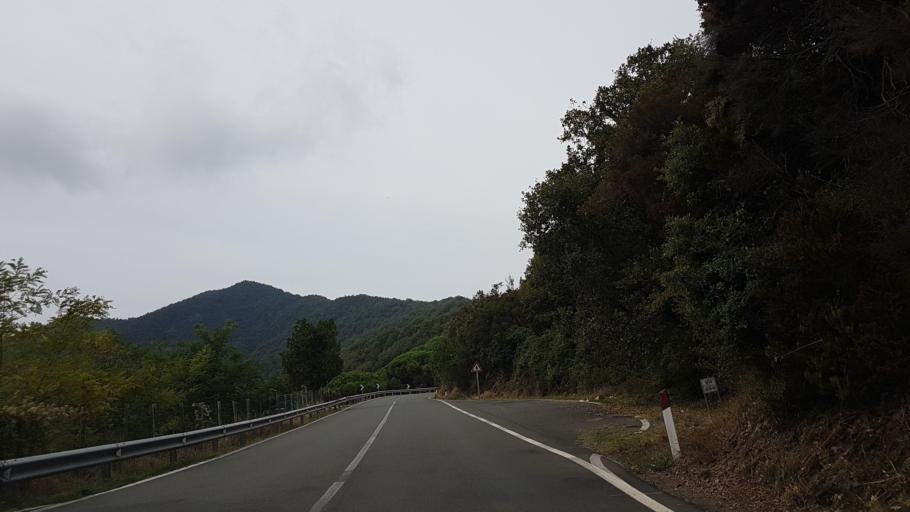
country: IT
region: Liguria
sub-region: Provincia di Genova
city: Moneglia
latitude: 44.2546
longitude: 9.4808
